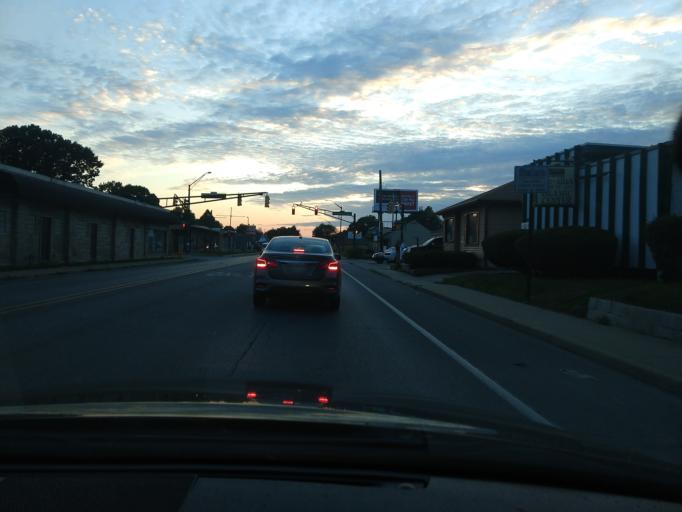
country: US
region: Indiana
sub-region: Marion County
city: Broad Ripple
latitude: 39.8403
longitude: -86.1259
